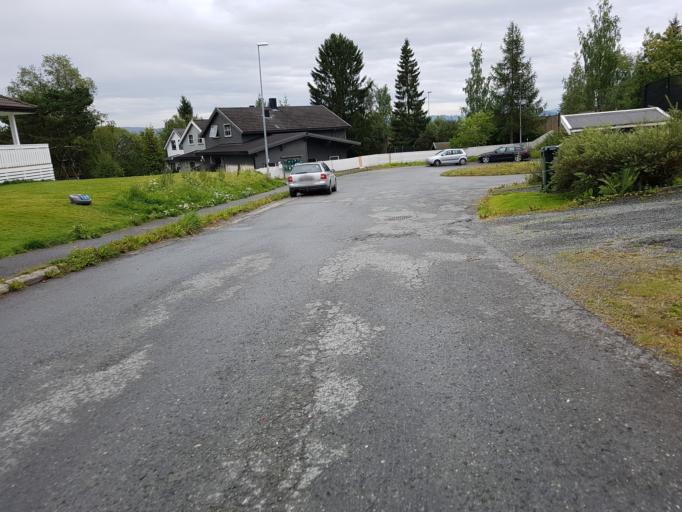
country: NO
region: Sor-Trondelag
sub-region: Trondheim
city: Trondheim
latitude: 63.3888
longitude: 10.3333
